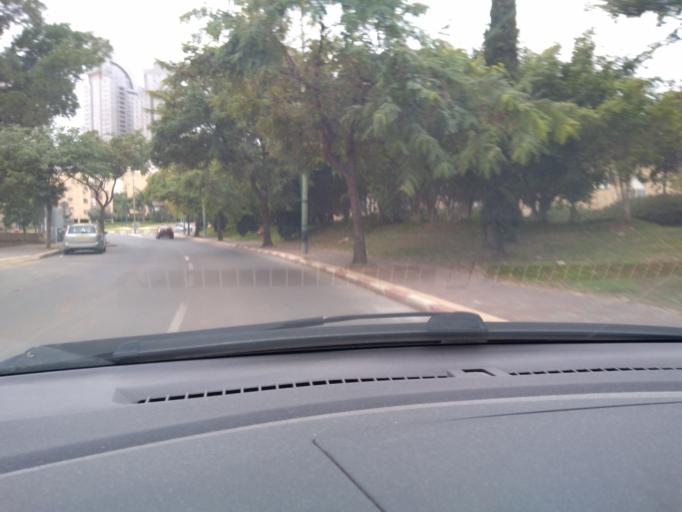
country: IL
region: Central District
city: Netanya
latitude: 32.3418
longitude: 34.8566
